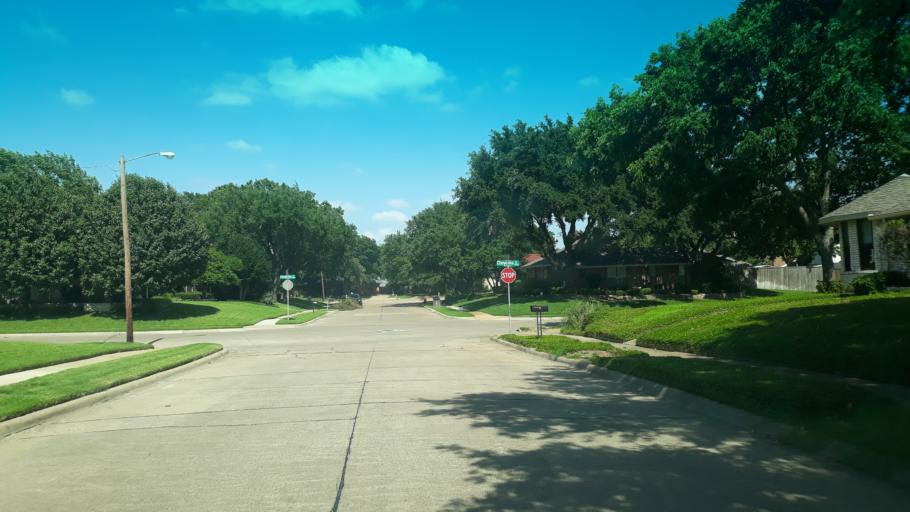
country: US
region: Texas
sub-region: Dallas County
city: Irving
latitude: 32.8591
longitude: -97.0023
